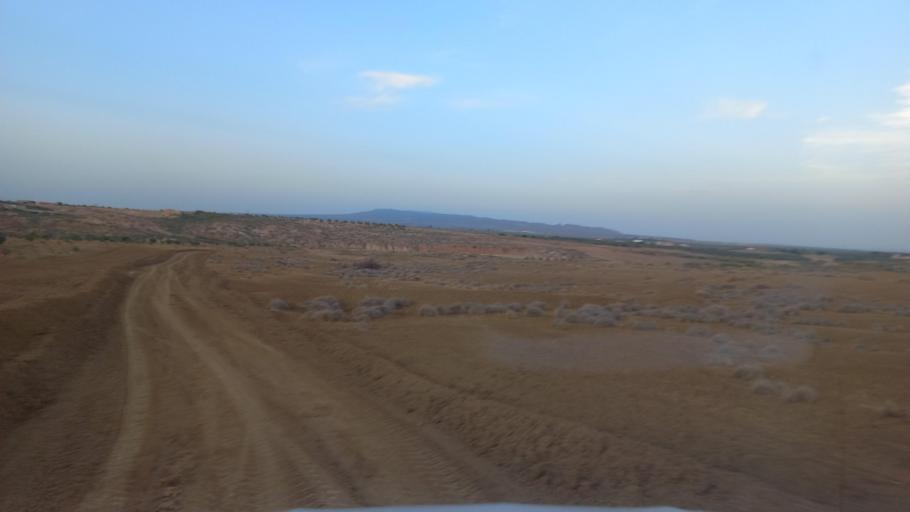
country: TN
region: Al Qasrayn
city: Kasserine
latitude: 35.2007
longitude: 9.0529
